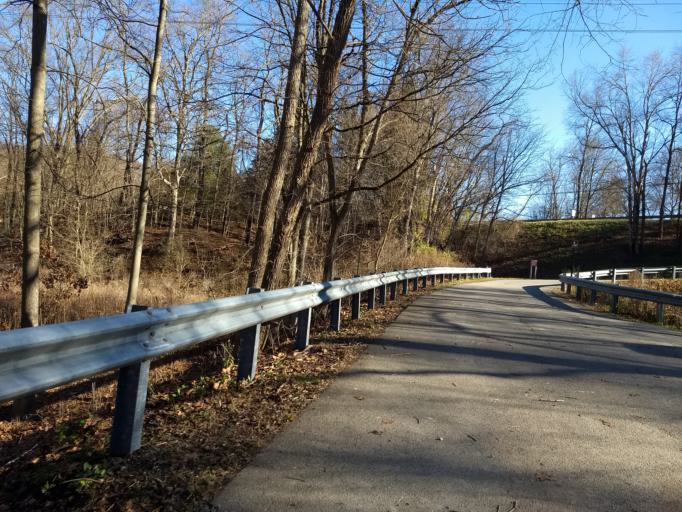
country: US
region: Pennsylvania
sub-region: Allegheny County
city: South Park Township
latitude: 40.2823
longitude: -79.9867
